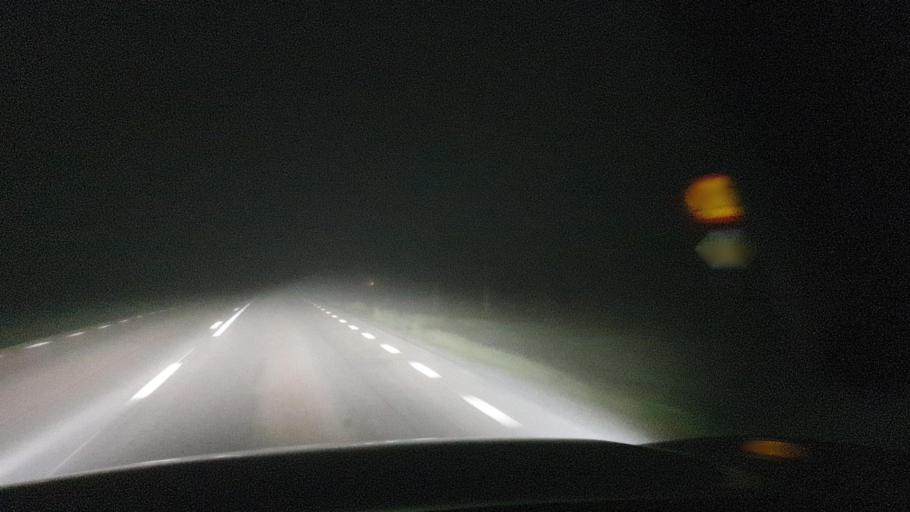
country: SE
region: Vaesternorrland
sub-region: Solleftea Kommun
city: Solleftea
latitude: 63.1690
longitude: 17.4276
